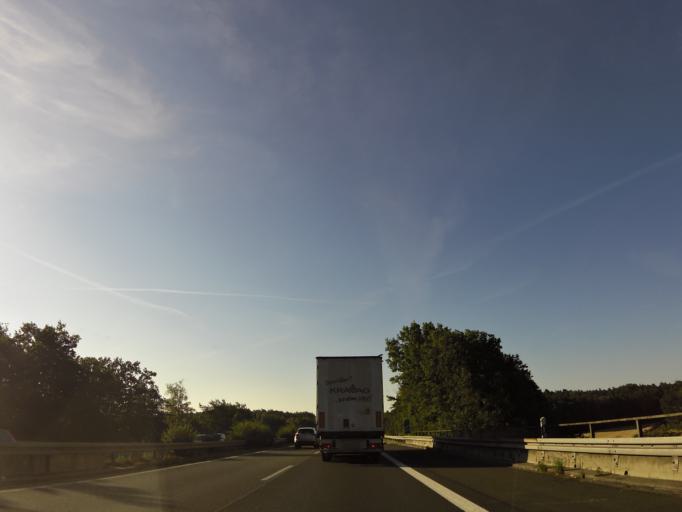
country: DE
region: Bavaria
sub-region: Regierungsbezirk Mittelfranken
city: Hochstadt an der Aisch
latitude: 49.7291
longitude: 10.8188
